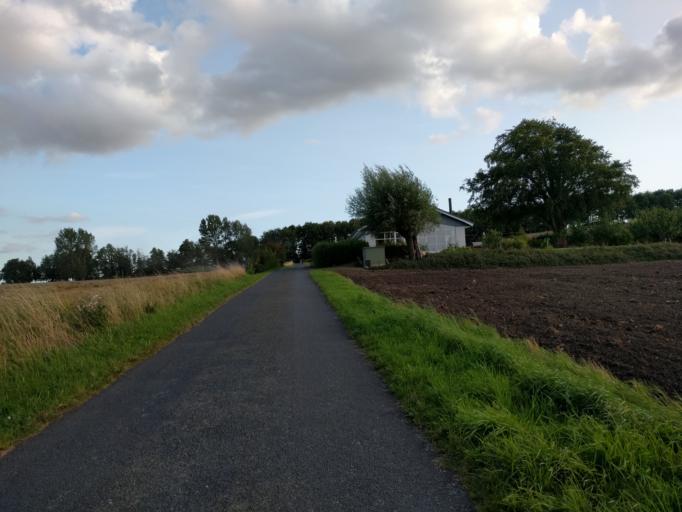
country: DK
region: South Denmark
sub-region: Kerteminde Kommune
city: Munkebo
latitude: 55.4699
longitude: 10.5801
